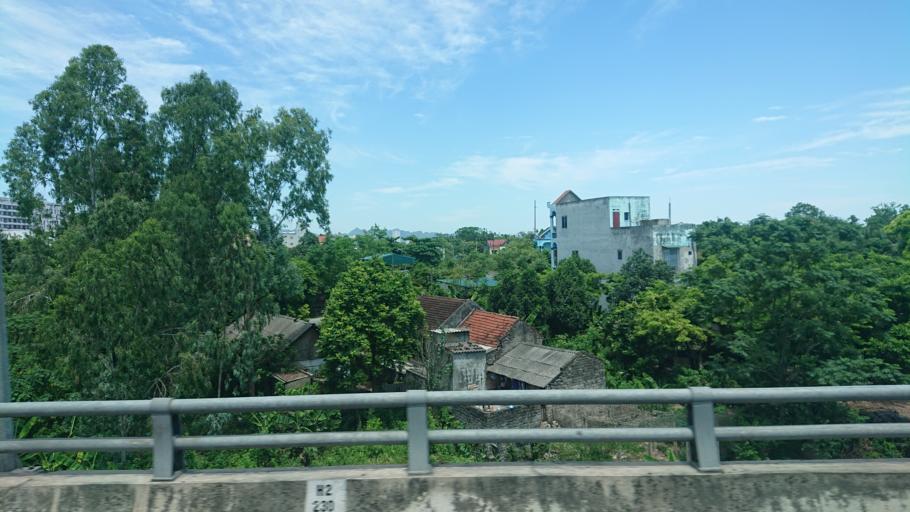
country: VN
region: Ha Nam
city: Thanh Pho Phu Ly
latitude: 20.5438
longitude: 105.9479
